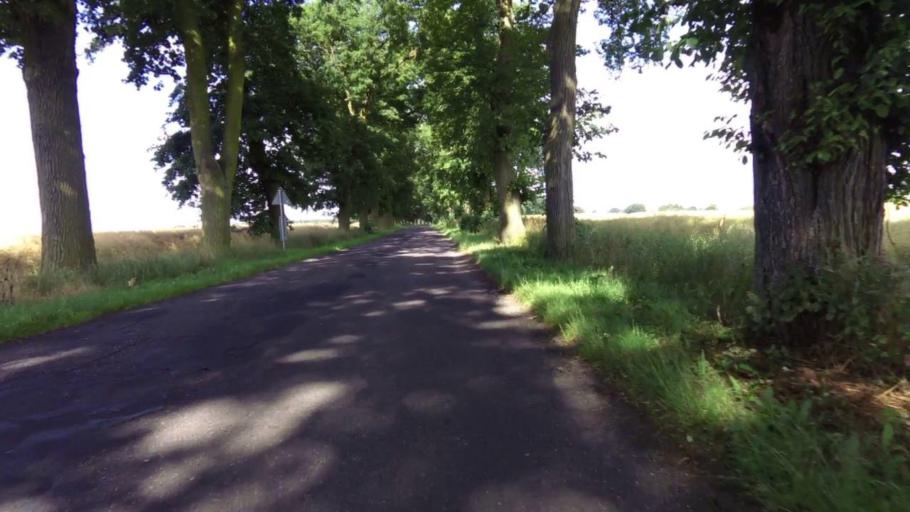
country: PL
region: West Pomeranian Voivodeship
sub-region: Powiat stargardzki
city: Stara Dabrowa
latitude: 53.3412
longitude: 15.1716
